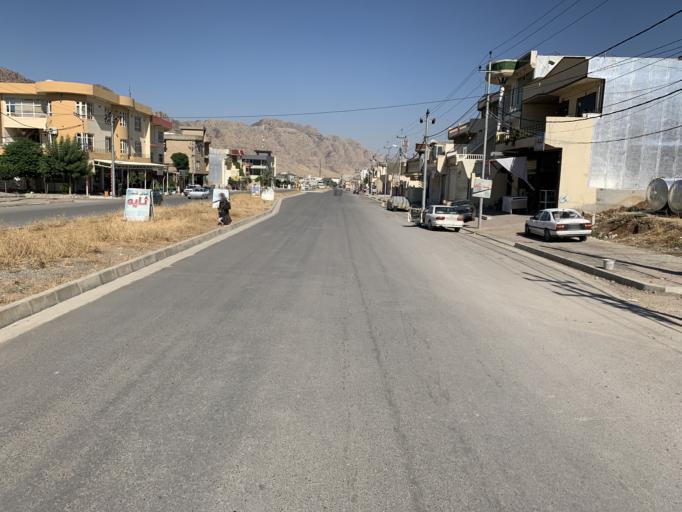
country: IQ
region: As Sulaymaniyah
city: Raniye
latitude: 36.2584
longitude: 44.8680
